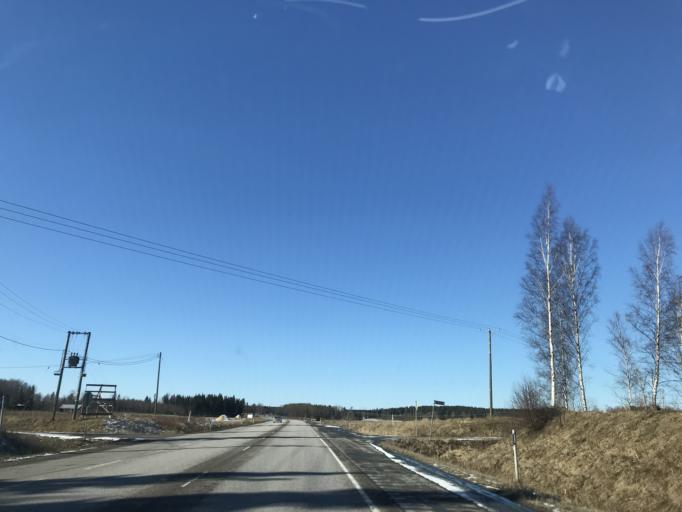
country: FI
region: Uusimaa
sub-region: Raaseporin
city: Inga
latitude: 60.0504
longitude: 23.9616
